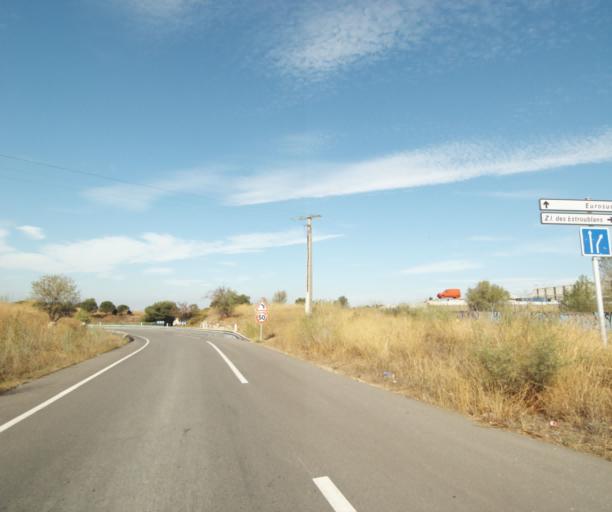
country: FR
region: Provence-Alpes-Cote d'Azur
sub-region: Departement des Bouches-du-Rhone
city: Saint-Victoret
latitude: 43.4251
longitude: 5.2375
